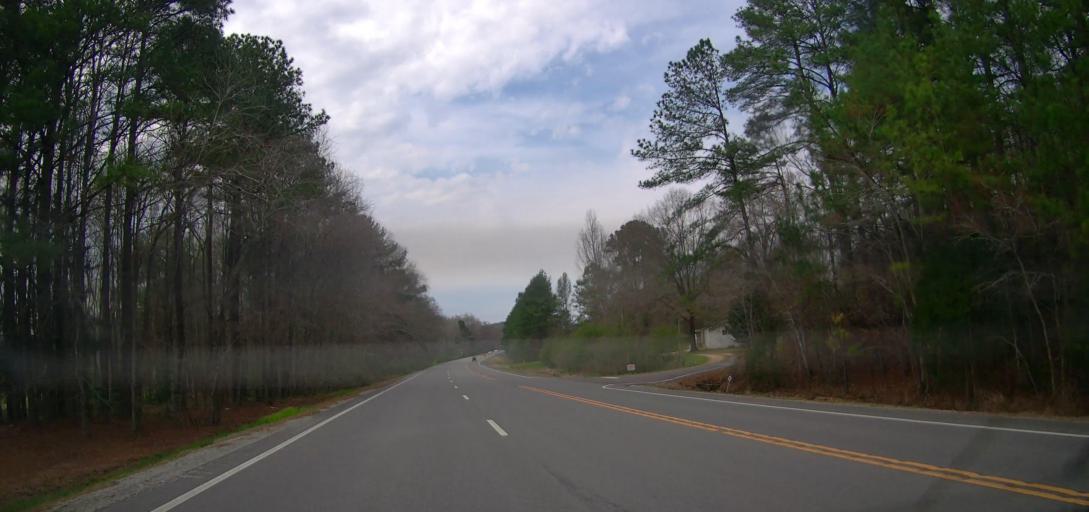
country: US
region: Alabama
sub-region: Marion County
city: Guin
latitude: 33.9908
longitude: -87.9261
